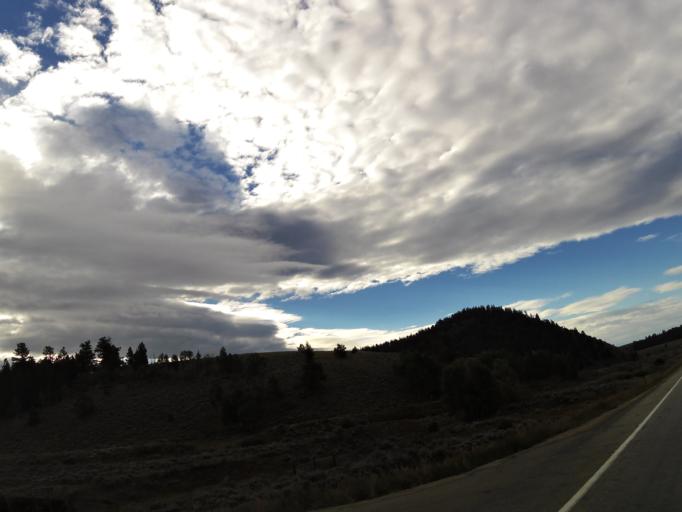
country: US
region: Colorado
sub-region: Chaffee County
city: Salida
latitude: 38.4049
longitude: -106.0676
